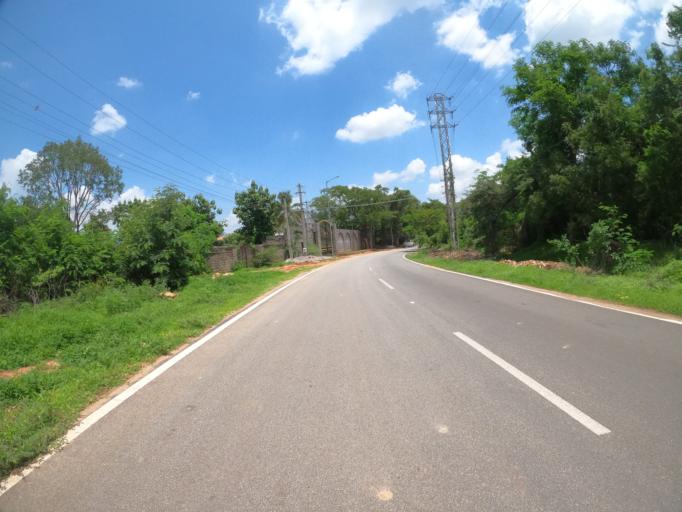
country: IN
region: Telangana
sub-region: Rangareddi
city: Sriramnagar
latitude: 17.3674
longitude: 78.3253
